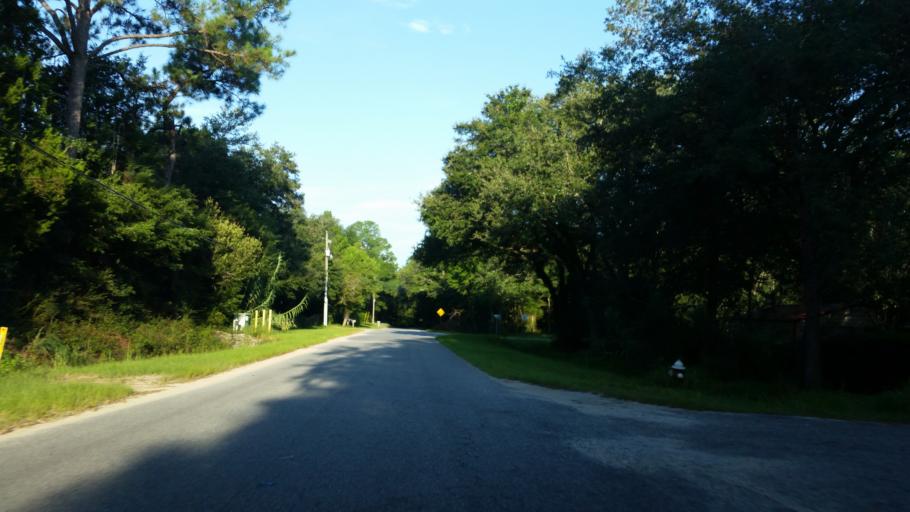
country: US
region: Florida
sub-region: Escambia County
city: Bellview
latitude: 30.4837
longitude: -87.3297
